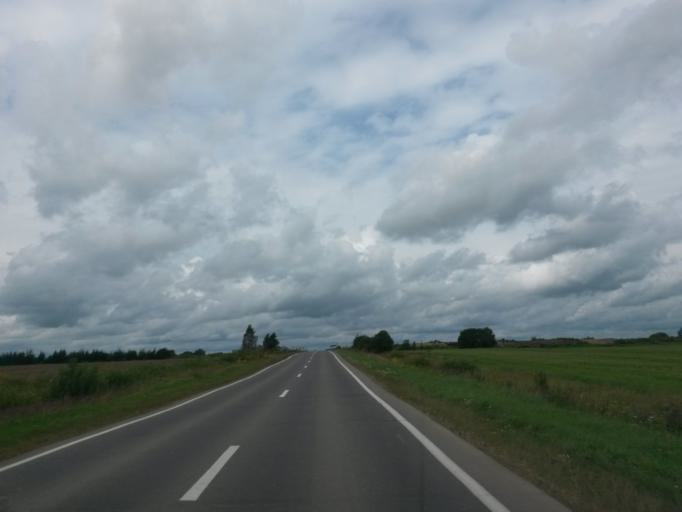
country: RU
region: Jaroslavl
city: Yaroslavl
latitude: 57.7494
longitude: 39.8792
